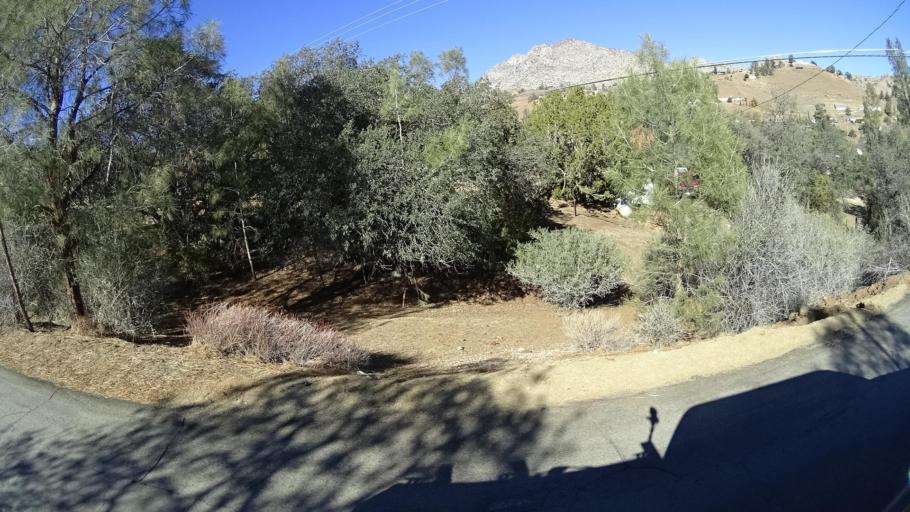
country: US
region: California
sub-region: Kern County
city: Wofford Heights
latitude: 35.7066
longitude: -118.4687
